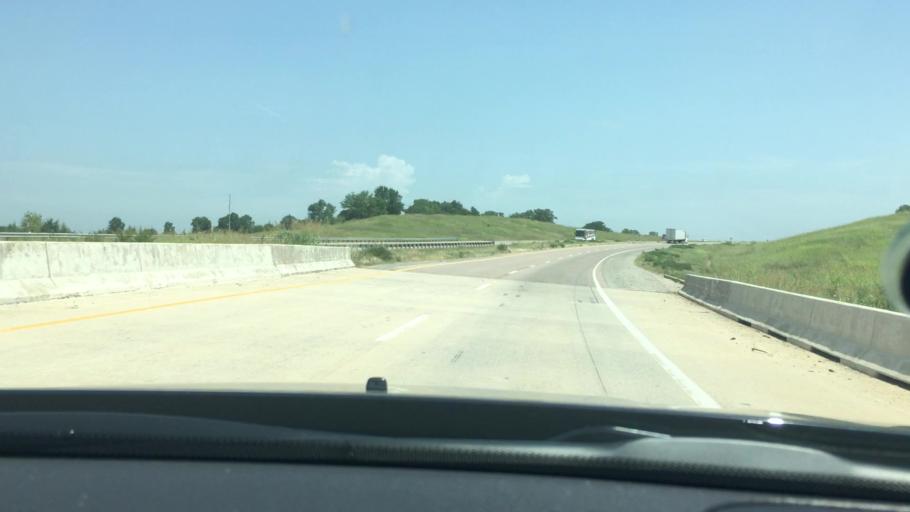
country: US
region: Oklahoma
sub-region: Pontotoc County
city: Ada
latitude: 34.8111
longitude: -96.6960
